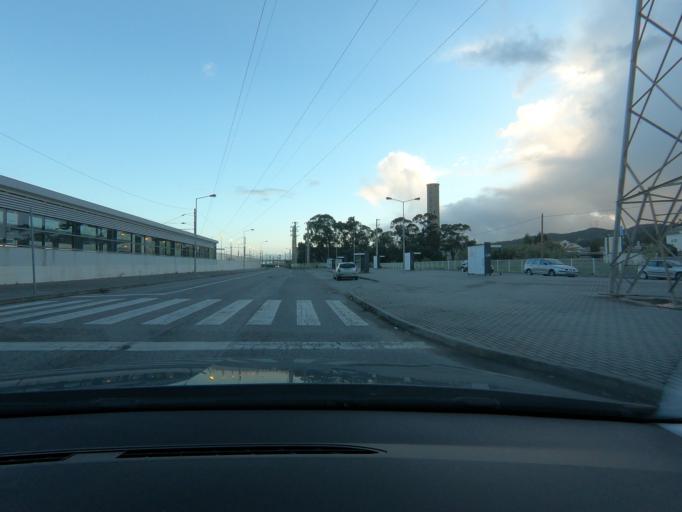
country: PT
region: Lisbon
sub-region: Vila Franca de Xira
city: Castanheira do Ribatejo
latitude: 38.9888
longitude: -8.9660
